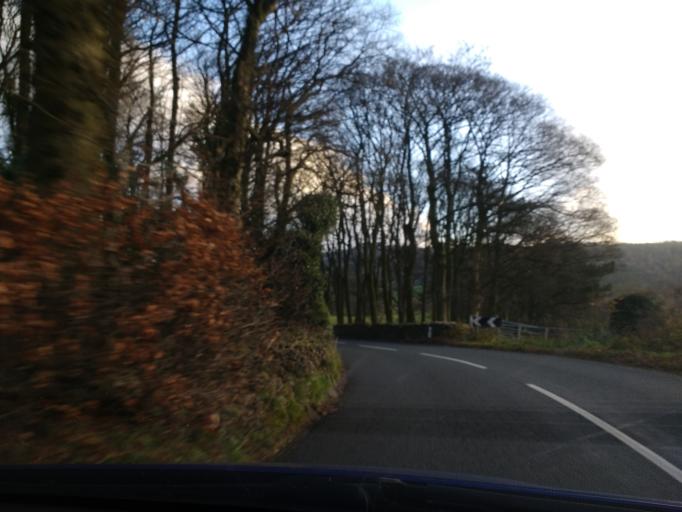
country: GB
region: England
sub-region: Lancashire
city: Caton
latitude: 54.0533
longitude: -2.7386
